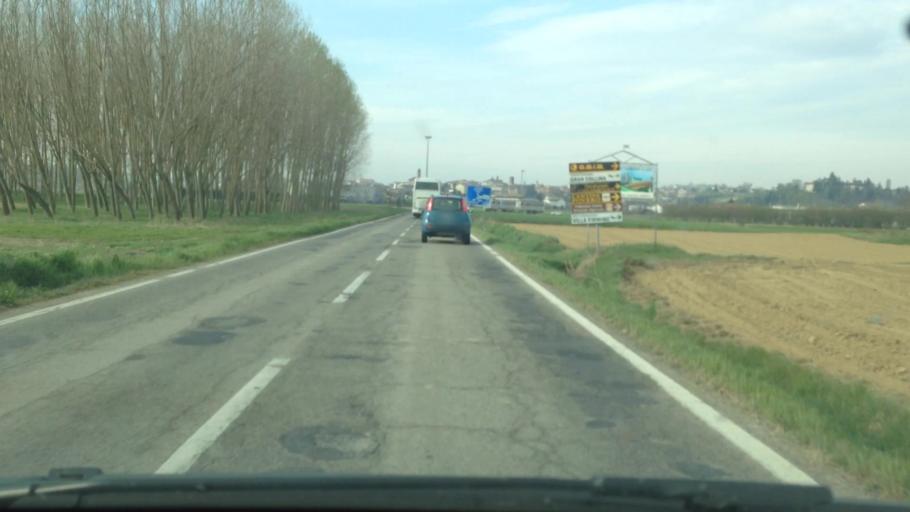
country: IT
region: Piedmont
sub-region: Provincia di Asti
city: San Damiano d'Asti
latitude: 44.8458
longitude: 8.0795
